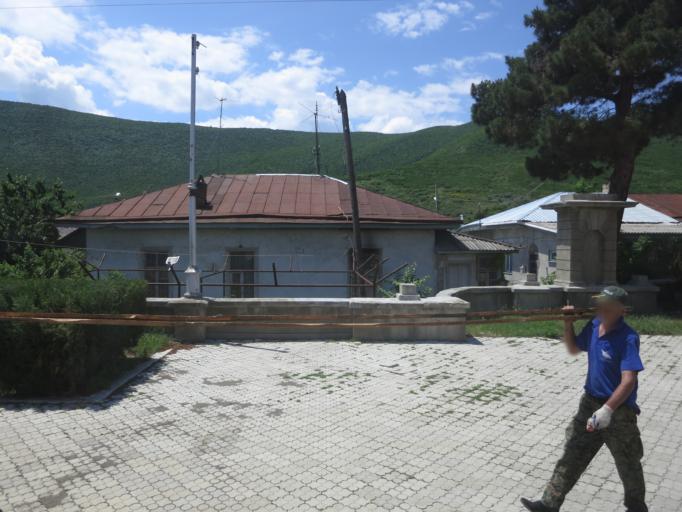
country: GE
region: Shida Kartli
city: Gori
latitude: 41.9723
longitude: 44.1097
